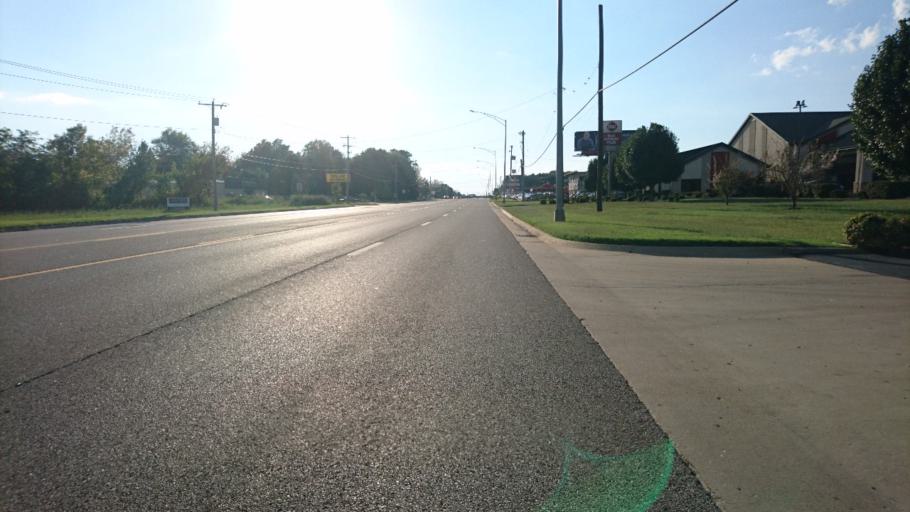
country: US
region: Missouri
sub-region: Greene County
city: Springfield
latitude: 37.2125
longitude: -93.3704
